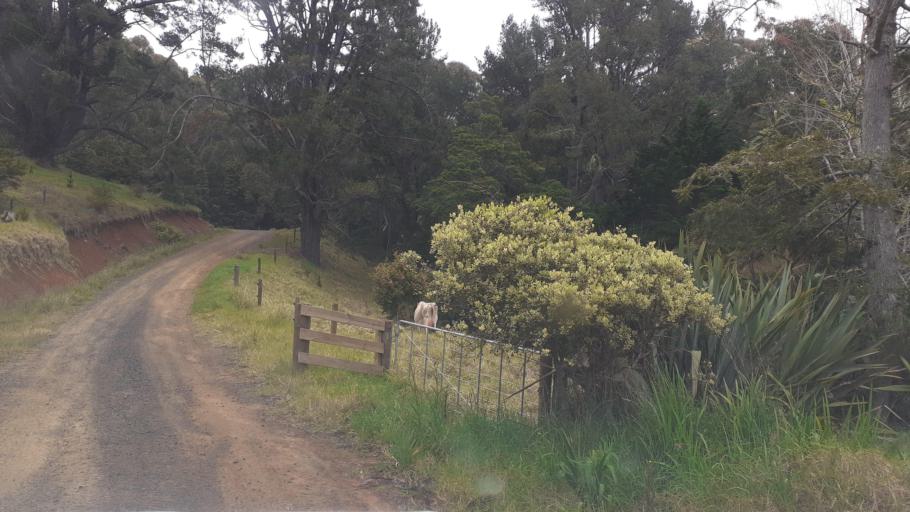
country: NZ
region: Northland
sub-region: Far North District
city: Kerikeri
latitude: -35.1036
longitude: 173.9257
